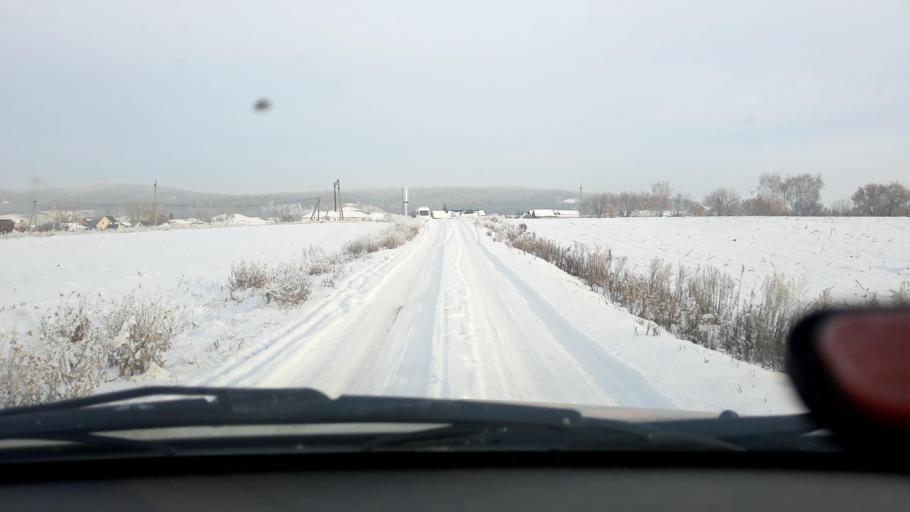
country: RU
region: Bashkortostan
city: Tolbazy
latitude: 54.3536
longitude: 55.8398
